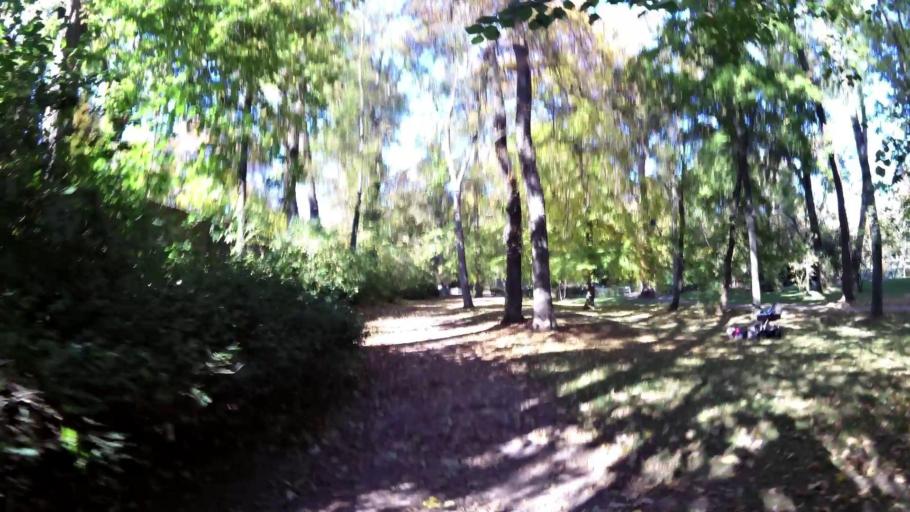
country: DE
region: Thuringia
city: Weimar
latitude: 50.9839
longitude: 11.3215
